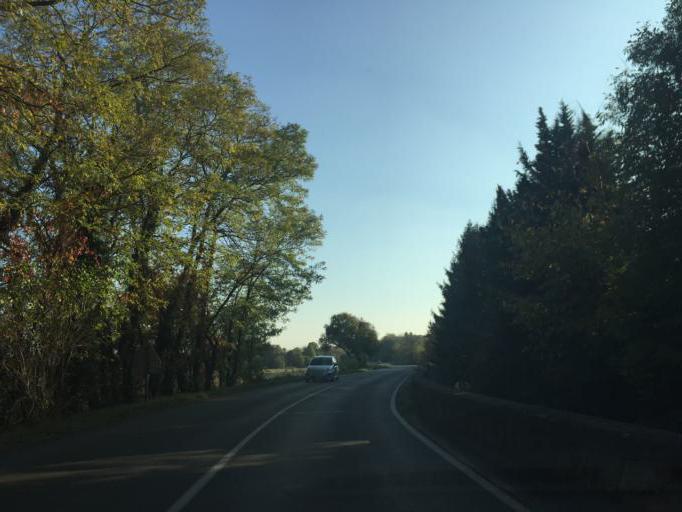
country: FR
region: Rhone-Alpes
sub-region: Departement de la Drome
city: Mours-Saint-Eusebe
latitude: 45.0664
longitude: 5.0406
